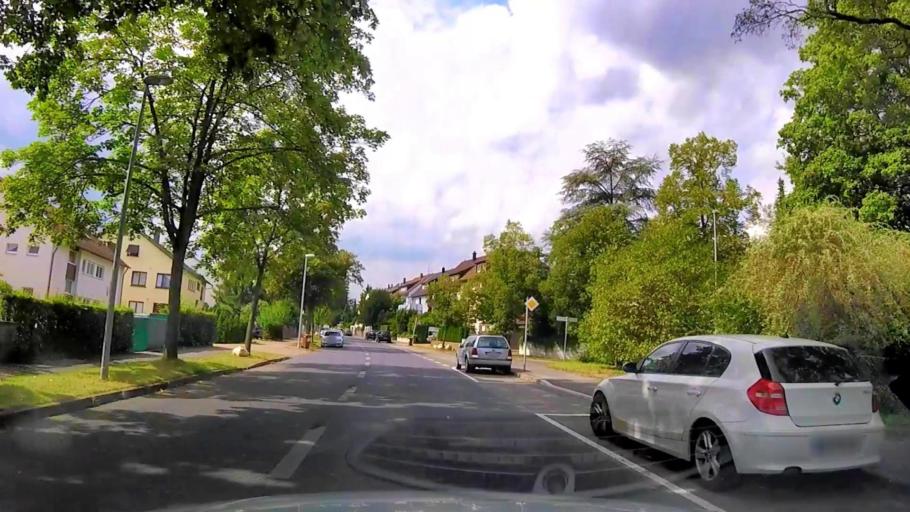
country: DE
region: Baden-Wuerttemberg
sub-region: Regierungsbezirk Stuttgart
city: Stuttgart Feuerbach
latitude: 48.8135
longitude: 9.1393
